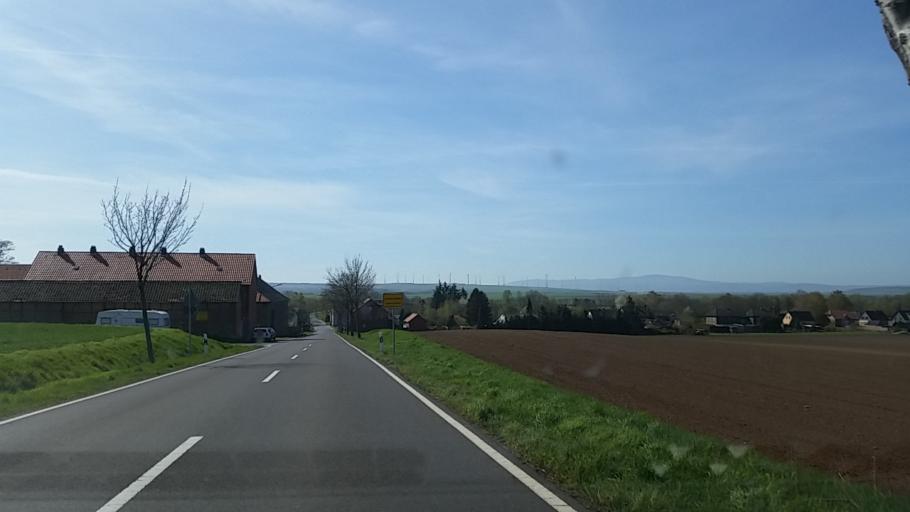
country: DE
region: Lower Saxony
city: Jerxheim
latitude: 52.0697
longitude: 10.8919
